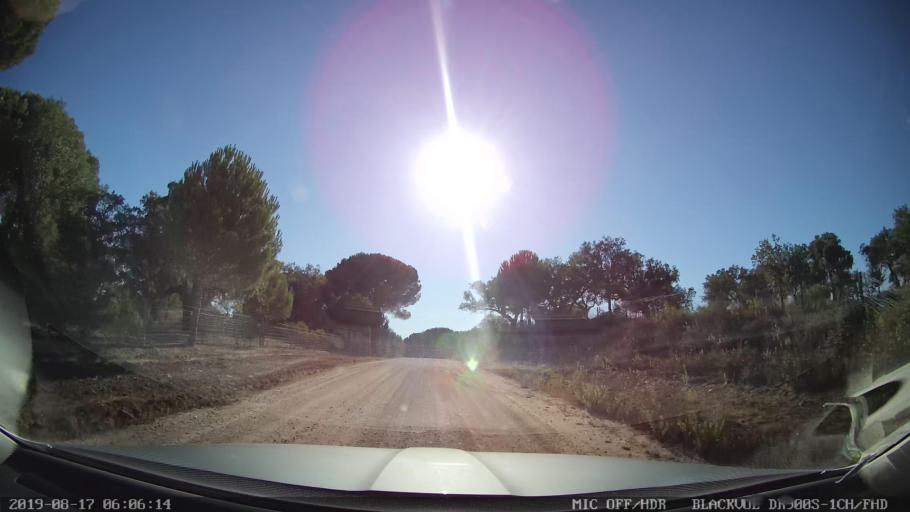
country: PT
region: Santarem
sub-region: Benavente
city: Poceirao
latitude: 38.8459
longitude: -8.6953
